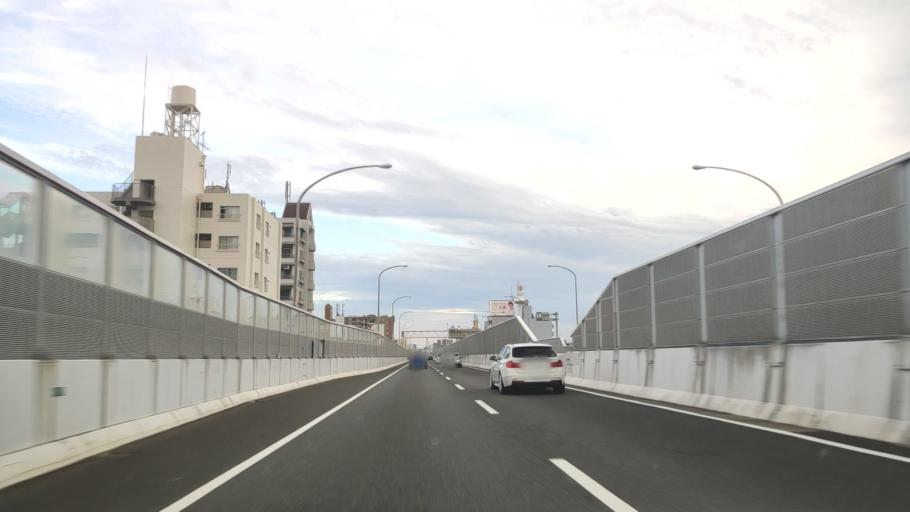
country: JP
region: Aichi
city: Nagoya-shi
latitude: 35.2118
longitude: 136.9108
